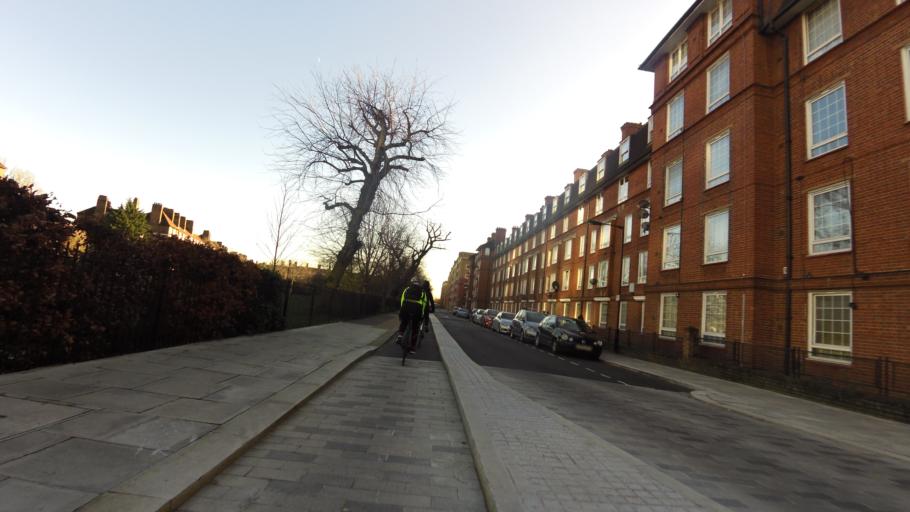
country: GB
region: England
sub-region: Greater London
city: City of London
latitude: 51.4991
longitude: -0.0903
